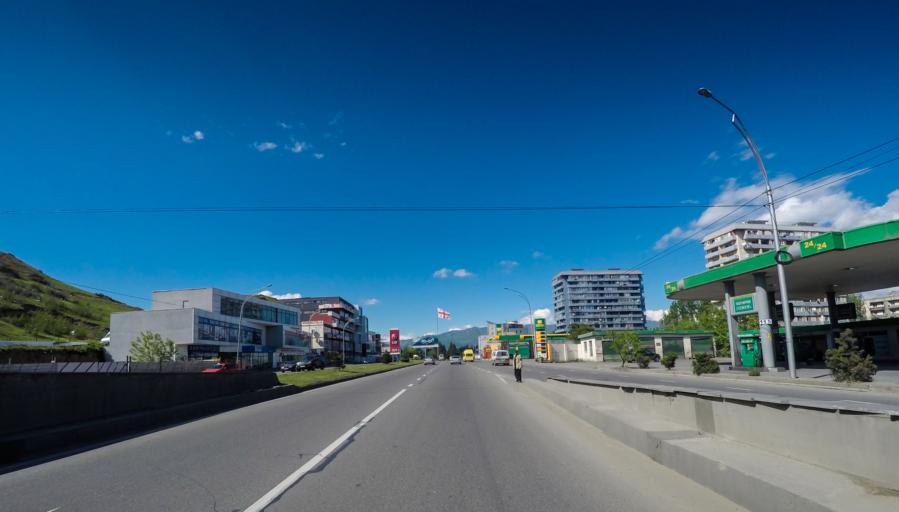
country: GE
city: Zahesi
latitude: 41.7639
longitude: 44.7688
